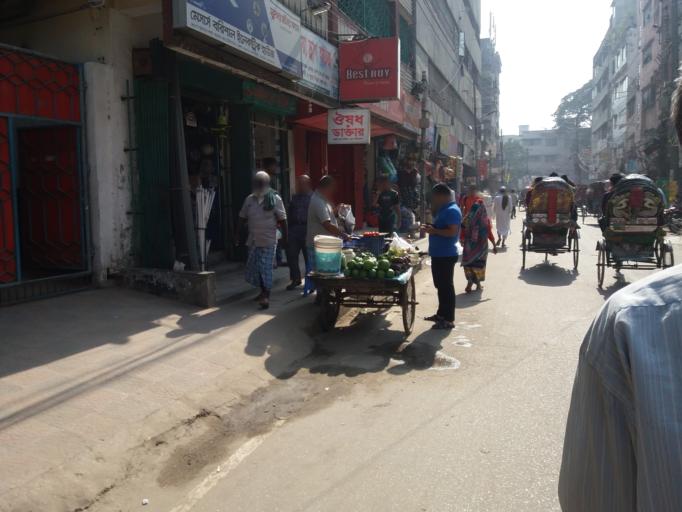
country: BD
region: Dhaka
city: Azimpur
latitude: 23.7390
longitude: 90.3723
